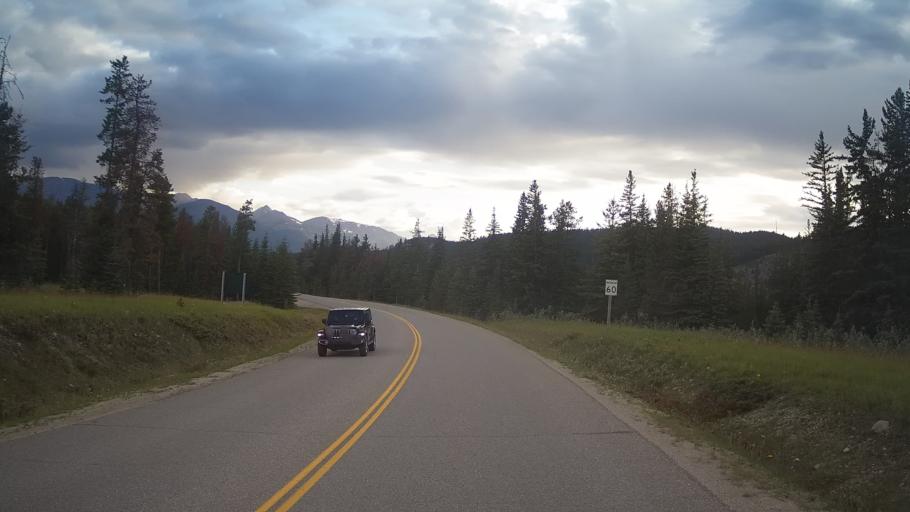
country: CA
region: Alberta
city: Jasper Park Lodge
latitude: 52.9220
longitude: -118.0379
